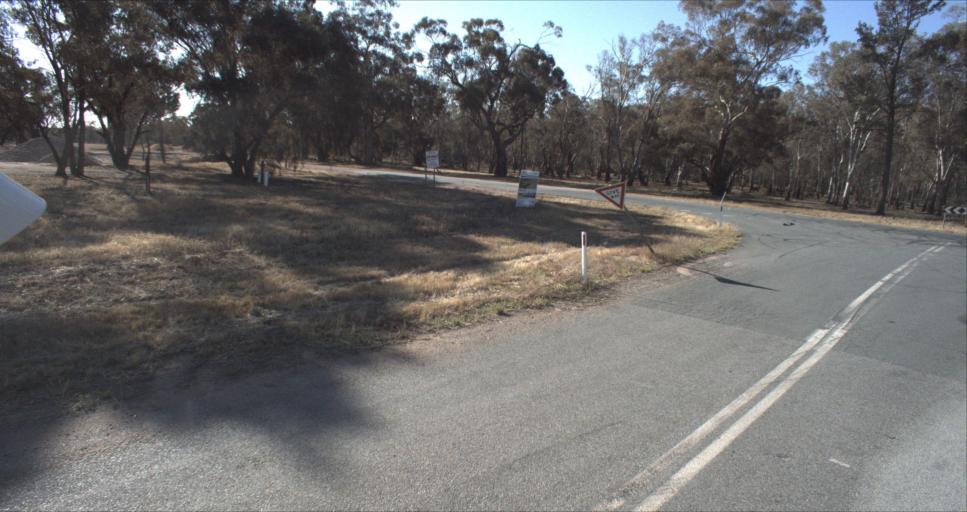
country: AU
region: New South Wales
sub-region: Leeton
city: Leeton
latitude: -34.6435
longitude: 146.3526
